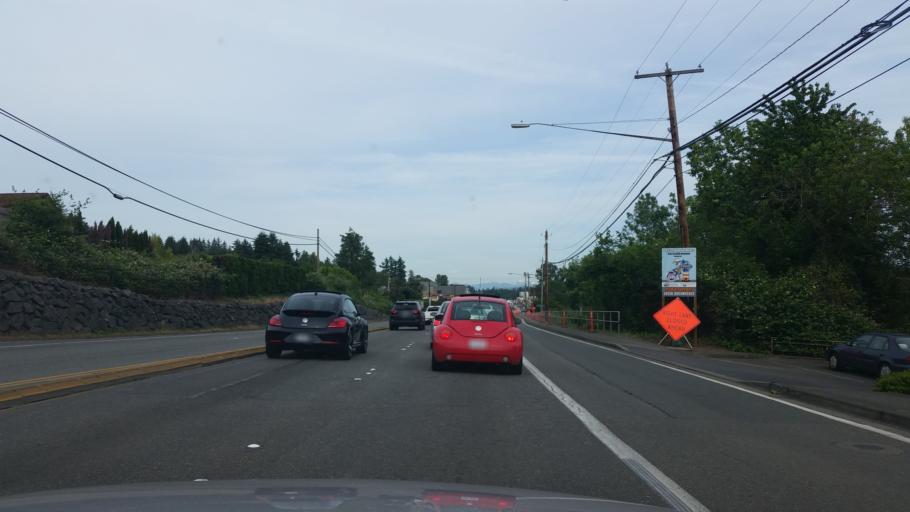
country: US
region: Washington
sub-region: King County
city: Lake Forest Park
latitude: 47.7581
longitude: -122.2669
